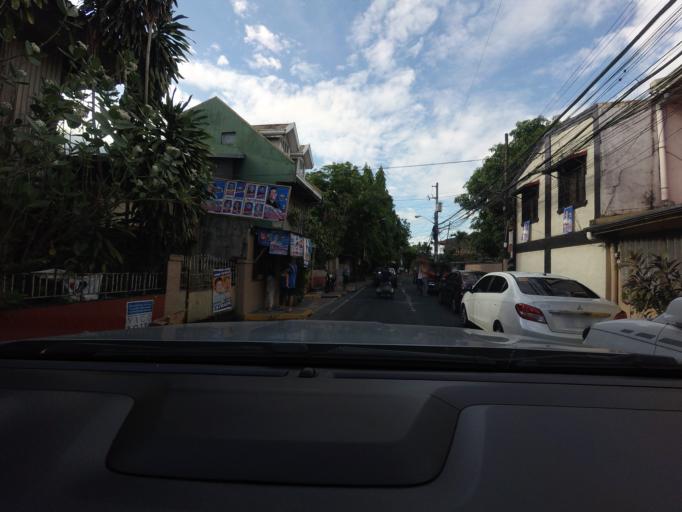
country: PH
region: Calabarzon
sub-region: Province of Rizal
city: Pateros
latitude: 14.5639
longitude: 121.0783
